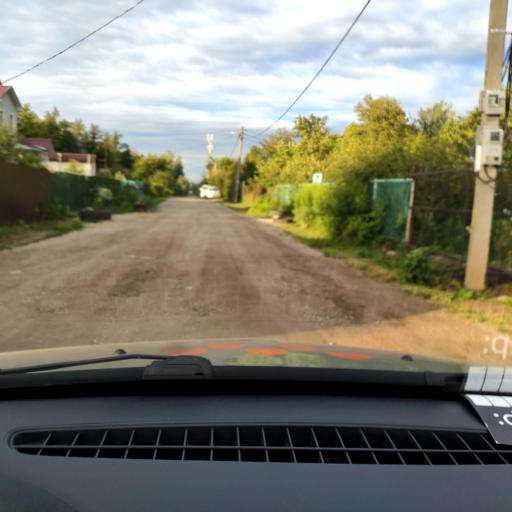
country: RU
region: Bashkortostan
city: Ufa
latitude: 54.6881
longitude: 55.8834
